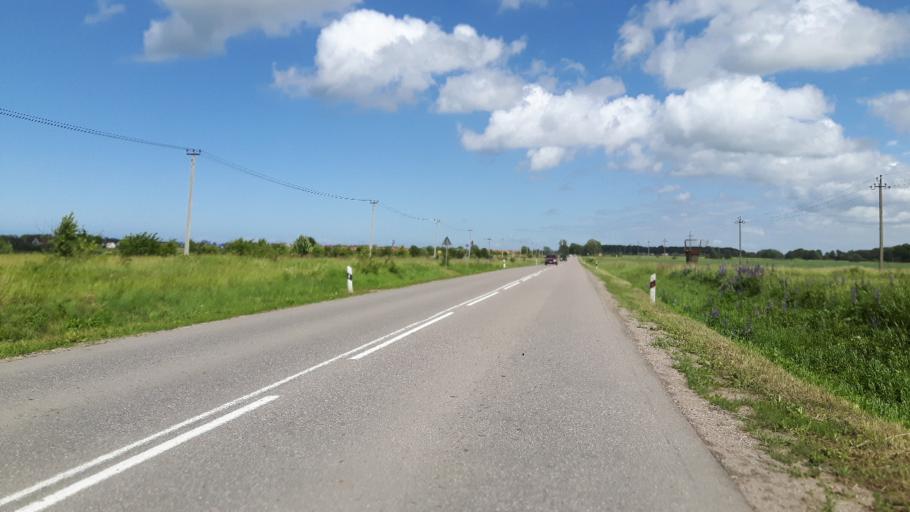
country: RU
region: Kaliningrad
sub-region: Zelenogradskiy Rayon
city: Zelenogradsk
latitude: 54.9294
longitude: 20.4240
